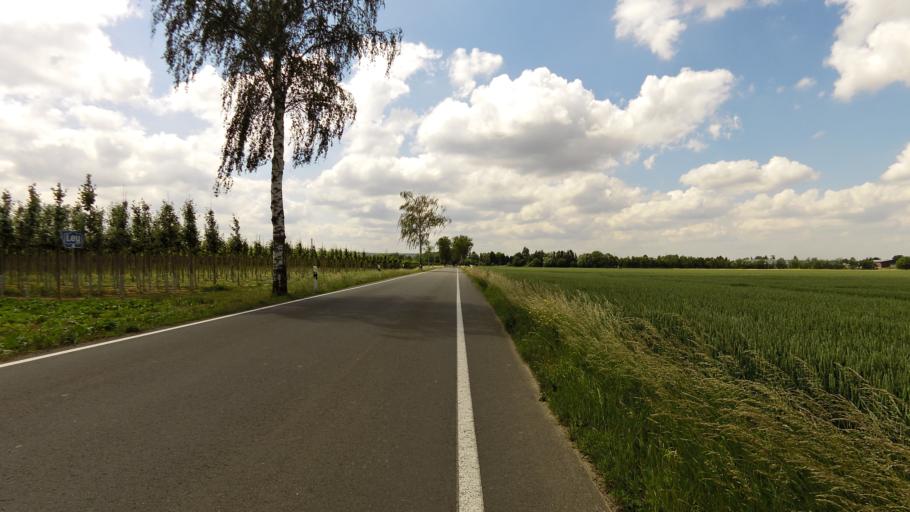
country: DE
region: North Rhine-Westphalia
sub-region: Regierungsbezirk Koln
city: Rheinbach
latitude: 50.6432
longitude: 6.9747
